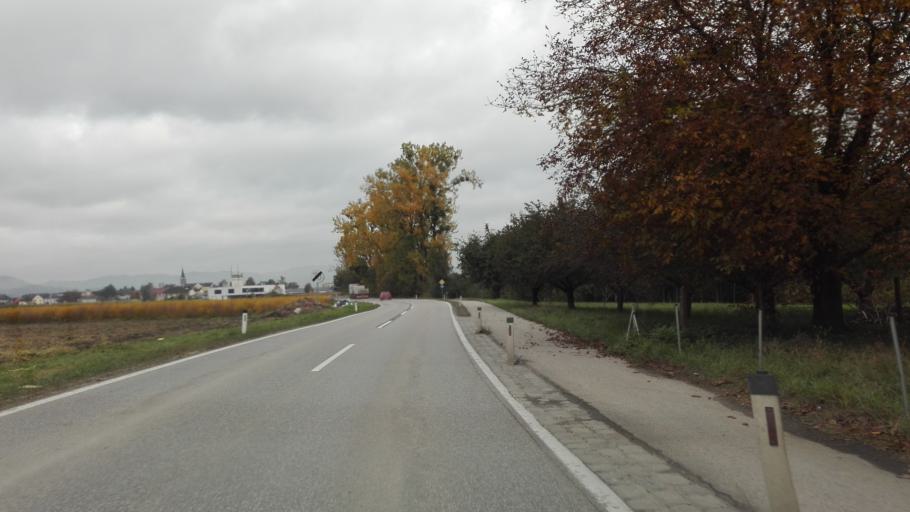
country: AT
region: Upper Austria
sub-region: Politischer Bezirk Urfahr-Umgebung
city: Feldkirchen an der Donau
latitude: 48.3307
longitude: 14.0068
